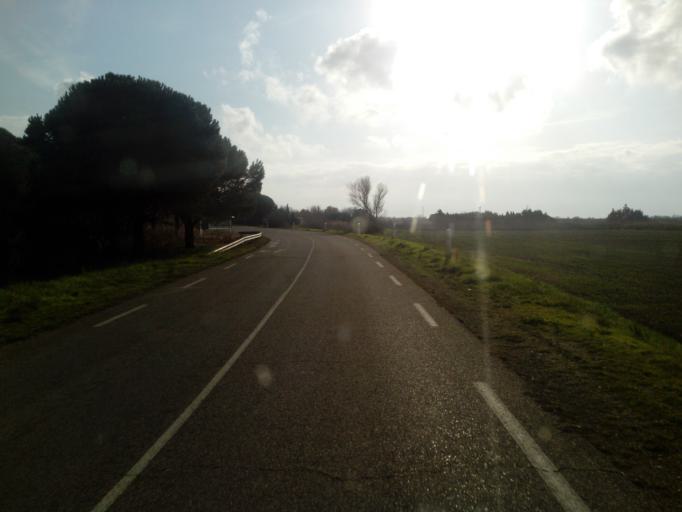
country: FR
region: Provence-Alpes-Cote d'Azur
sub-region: Departement des Bouches-du-Rhone
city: Port-Saint-Louis-du-Rhone
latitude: 43.4723
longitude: 4.7068
